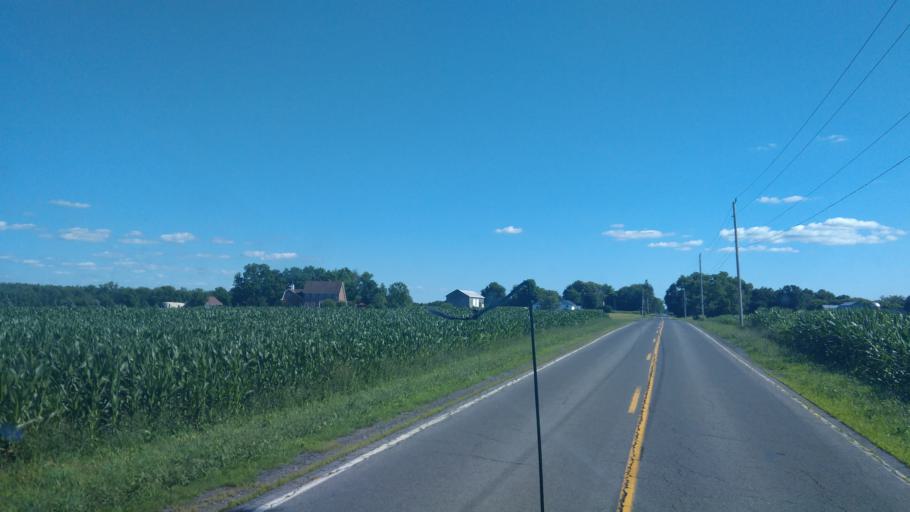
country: US
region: New York
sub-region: Seneca County
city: Seneca Falls
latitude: 42.9699
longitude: -76.7959
